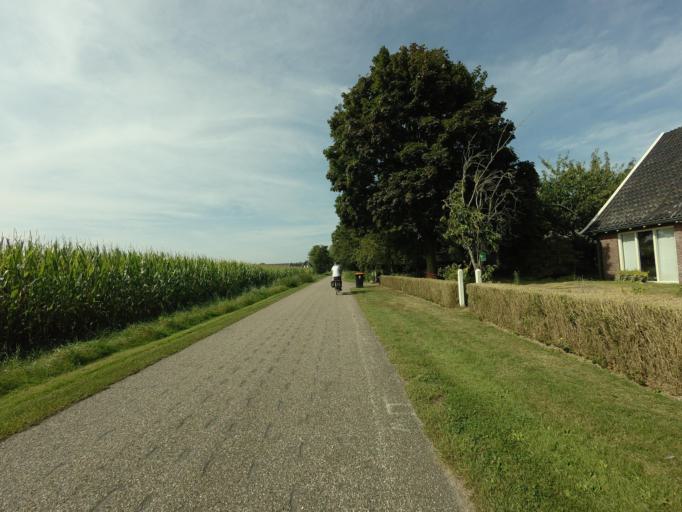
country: NL
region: Overijssel
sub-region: Gemeente Hof van Twente
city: Goor
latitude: 52.2567
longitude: 6.6001
